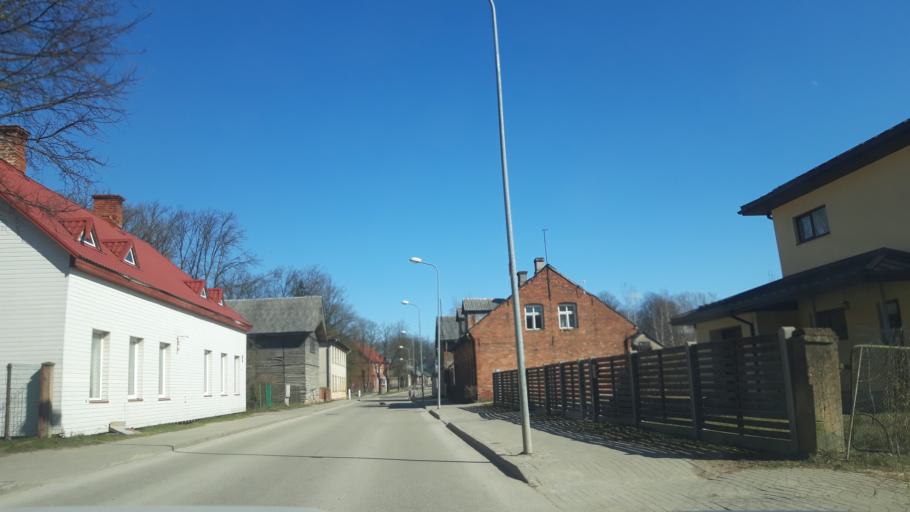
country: LV
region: Valmieras Rajons
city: Valmiera
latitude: 57.5335
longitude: 25.4130
